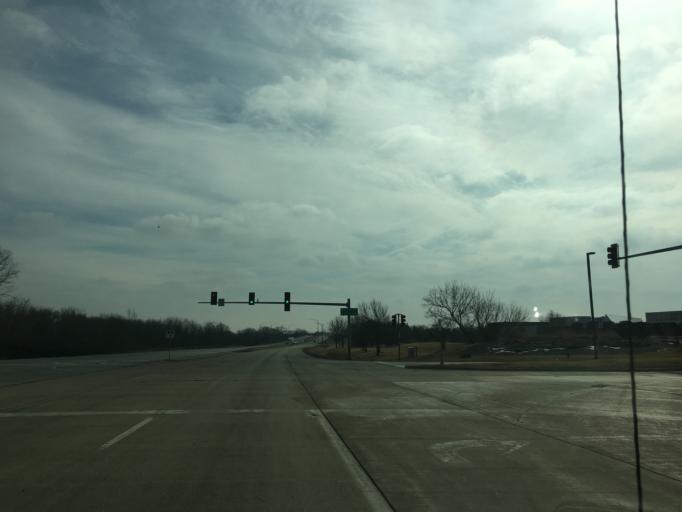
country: US
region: Illinois
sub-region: Kane County
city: Carpentersville
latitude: 42.0799
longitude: -88.2103
